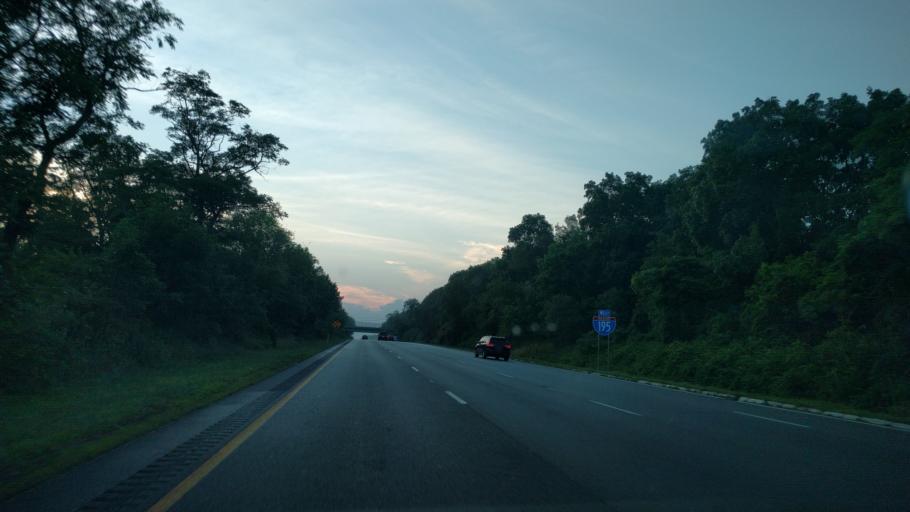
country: US
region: Massachusetts
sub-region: Bristol County
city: Ocean Grove
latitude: 41.7530
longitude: -71.2215
